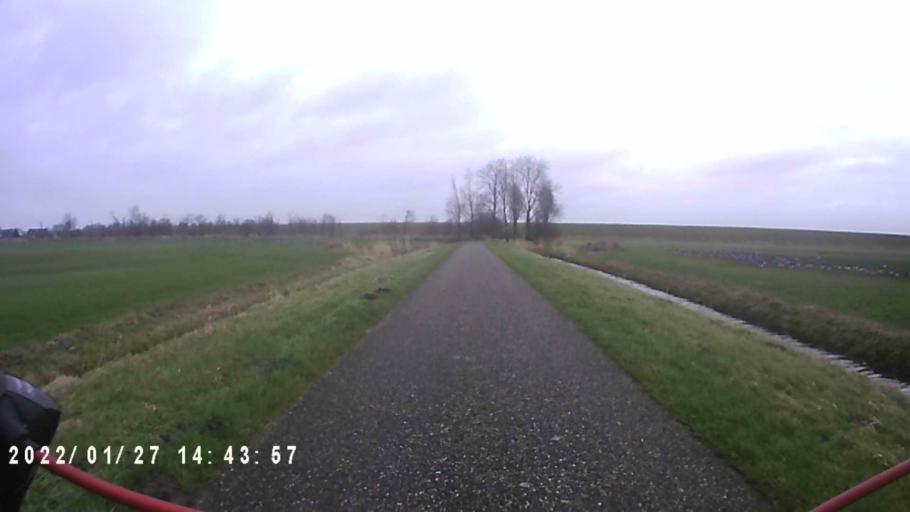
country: NL
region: Friesland
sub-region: Gemeente Dongeradeel
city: Anjum
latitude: 53.3551
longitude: 6.1415
